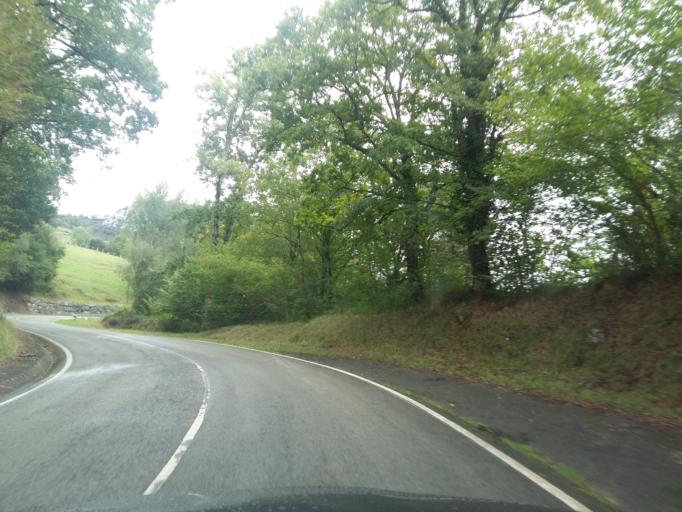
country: ES
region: Basque Country
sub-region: Bizkaia
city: Lanestosa
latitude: 43.1864
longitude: -3.5149
